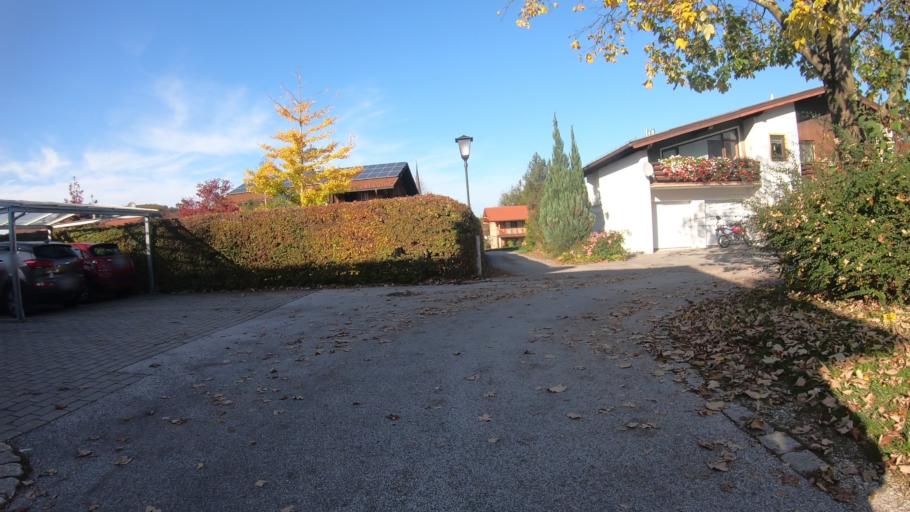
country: DE
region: Bavaria
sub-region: Upper Bavaria
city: Bergen
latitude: 47.8050
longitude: 12.5900
